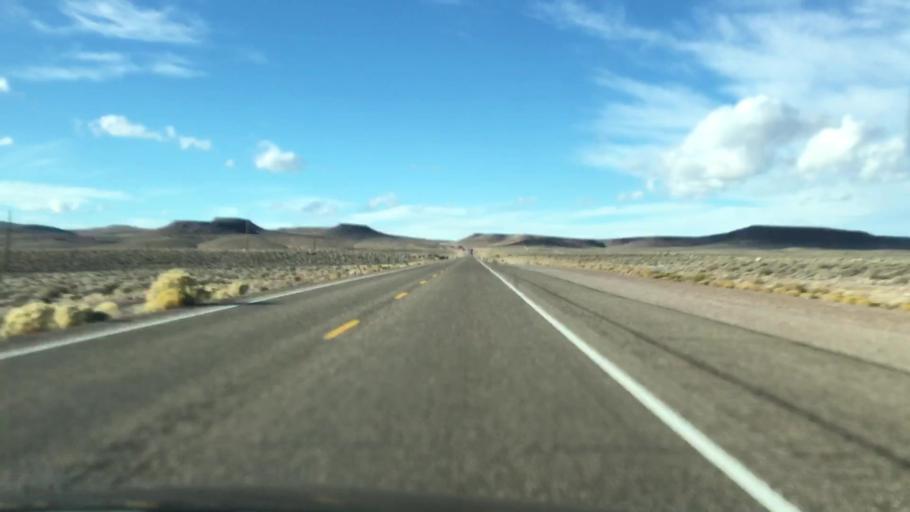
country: US
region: Nevada
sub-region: Esmeralda County
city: Goldfield
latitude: 37.3675
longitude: -117.1230
